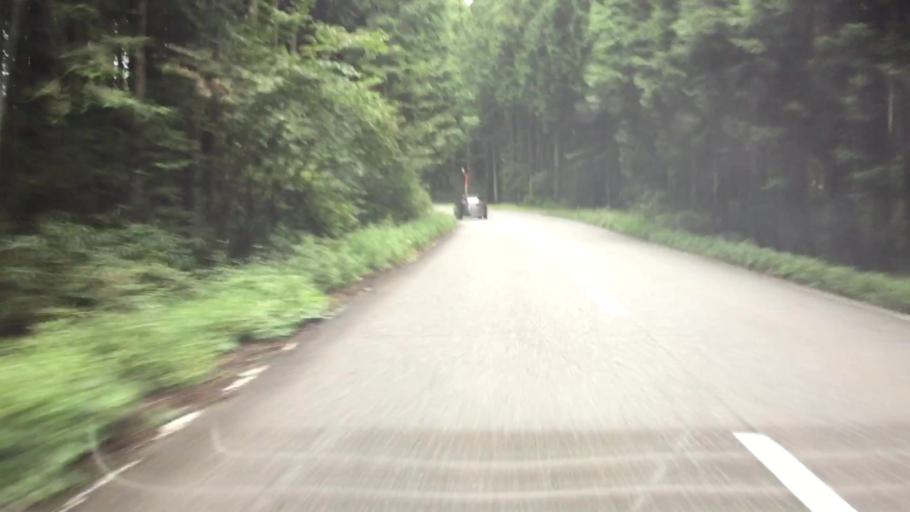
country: JP
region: Tochigi
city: Imaichi
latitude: 36.7695
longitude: 139.7046
